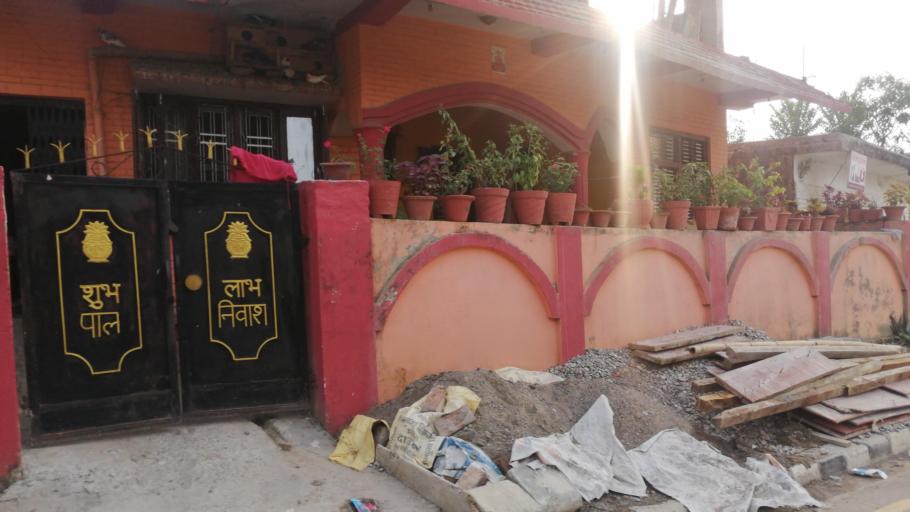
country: NP
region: Western Region
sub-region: Lumbini Zone
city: Bhairahawa
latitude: 27.4999
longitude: 83.4505
